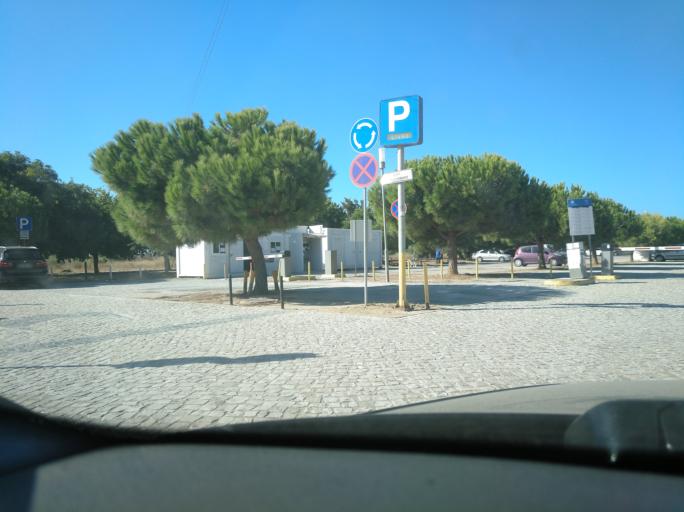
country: PT
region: Faro
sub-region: Vila Real de Santo Antonio
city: Monte Gordo
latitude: 37.1651
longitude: -7.5208
